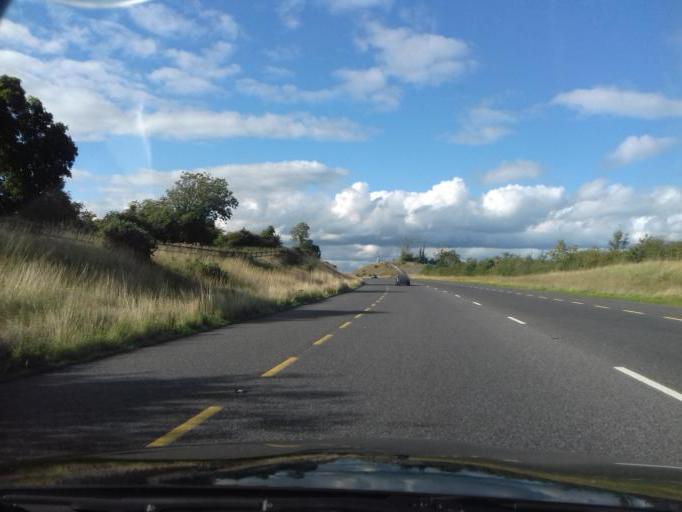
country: IE
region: Leinster
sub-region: Uibh Fhaili
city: Tullamore
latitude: 53.2974
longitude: -7.4832
